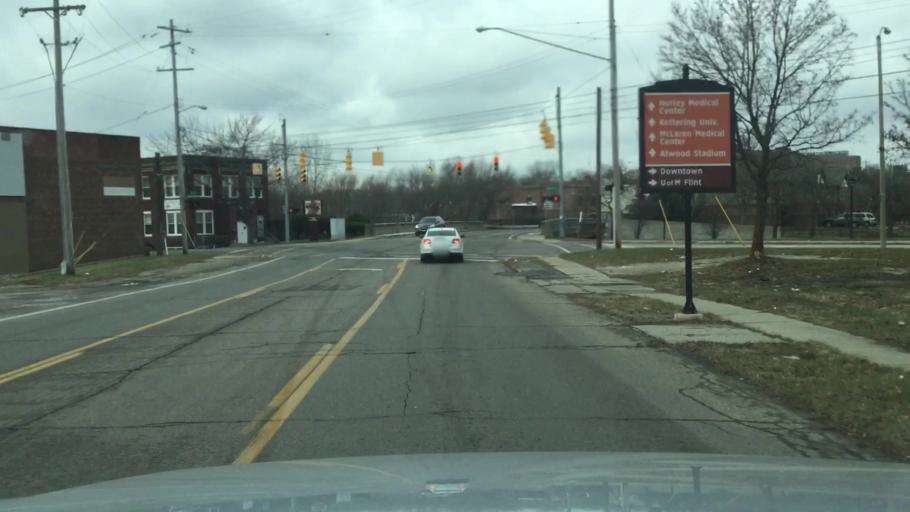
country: US
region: Michigan
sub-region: Genesee County
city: Flint
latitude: 43.0146
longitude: -83.6952
